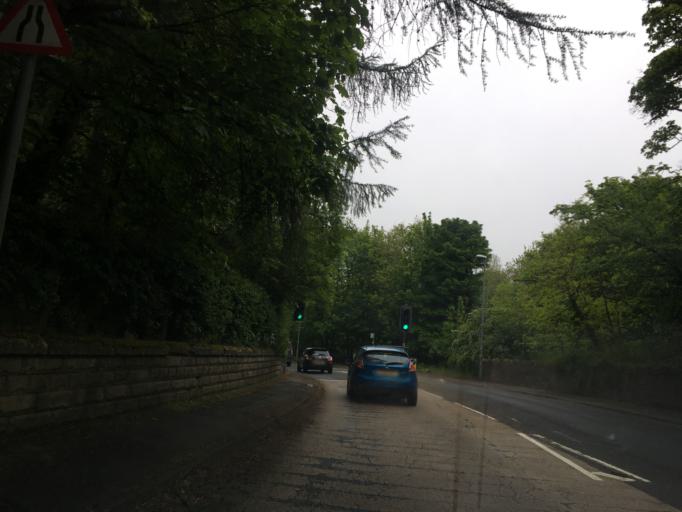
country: GB
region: Scotland
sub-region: Midlothian
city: Penicuik
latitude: 55.8442
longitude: -3.1933
